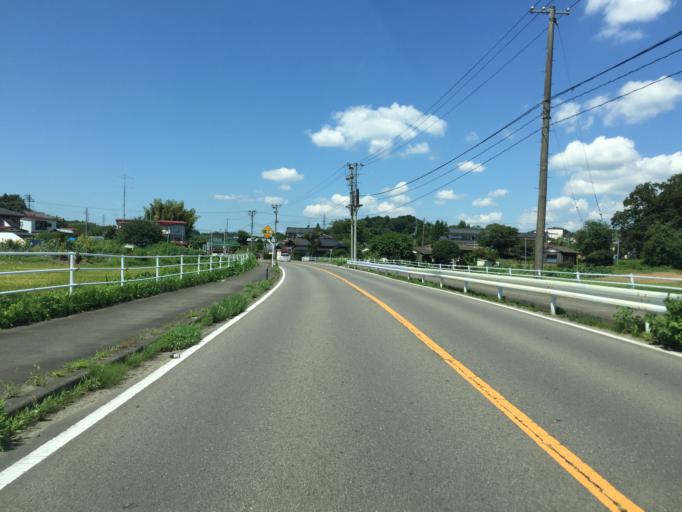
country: JP
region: Fukushima
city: Nihommatsu
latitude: 37.6222
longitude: 140.4624
